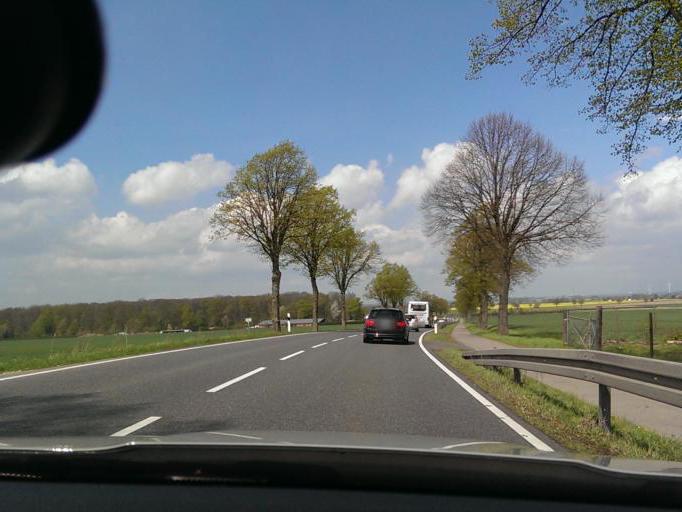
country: DE
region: Lower Saxony
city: Nordstemmen
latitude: 52.1975
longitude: 9.7467
